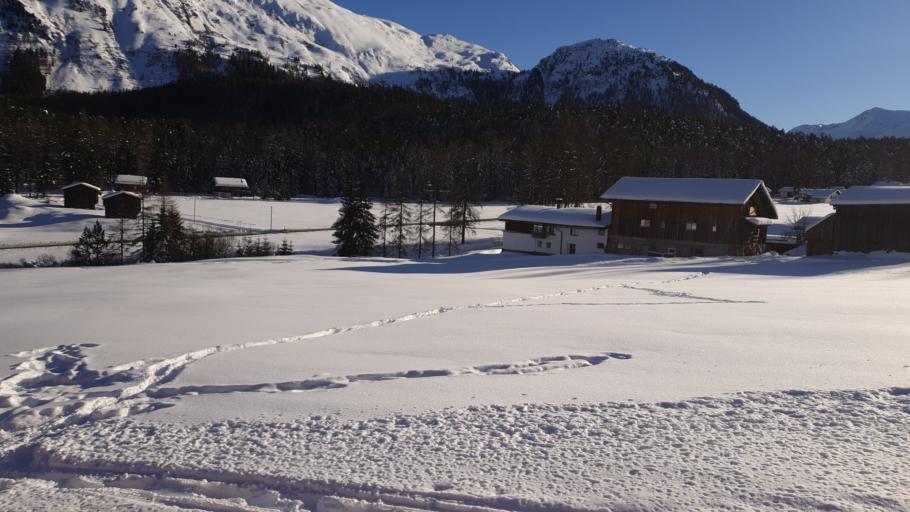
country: CH
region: Grisons
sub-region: Praettigau/Davos District
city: Davos
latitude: 46.8406
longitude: 9.8566
